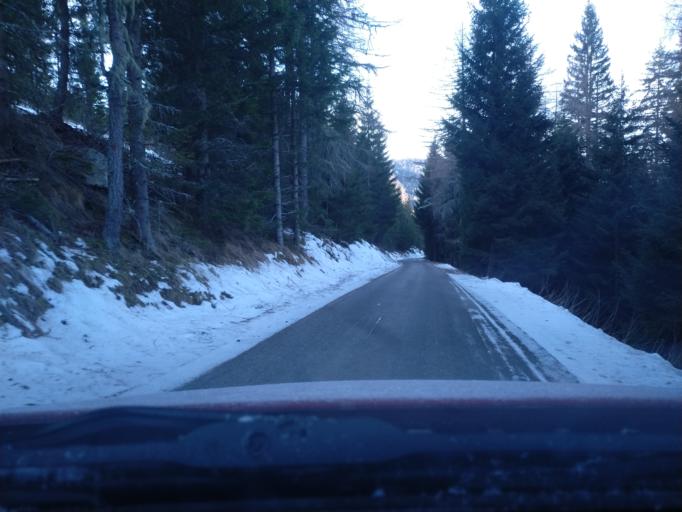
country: AT
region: Carinthia
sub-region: Politischer Bezirk Villach Land
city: Arriach
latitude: 46.7117
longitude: 13.8986
